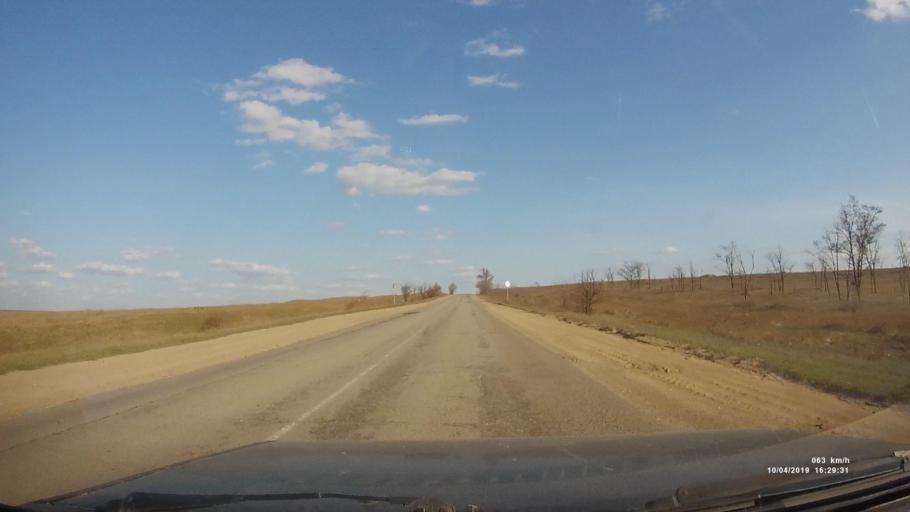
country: RU
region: Rostov
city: Staraya Stanitsa
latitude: 48.2680
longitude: 40.3561
